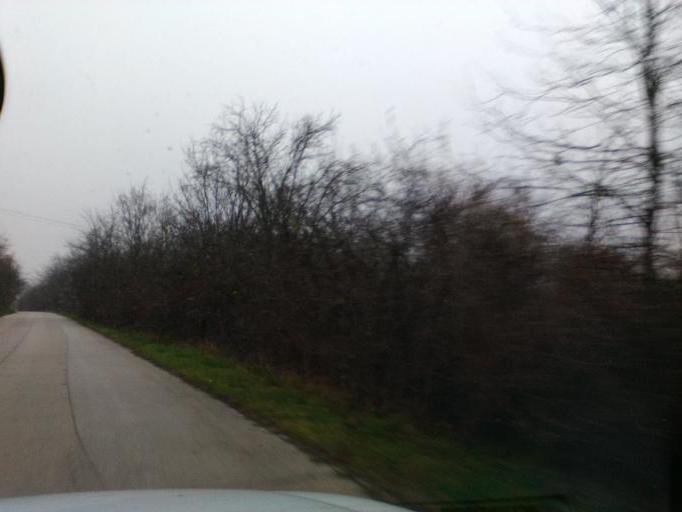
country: HU
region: Pest
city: Soskut
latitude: 47.3997
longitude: 18.7876
